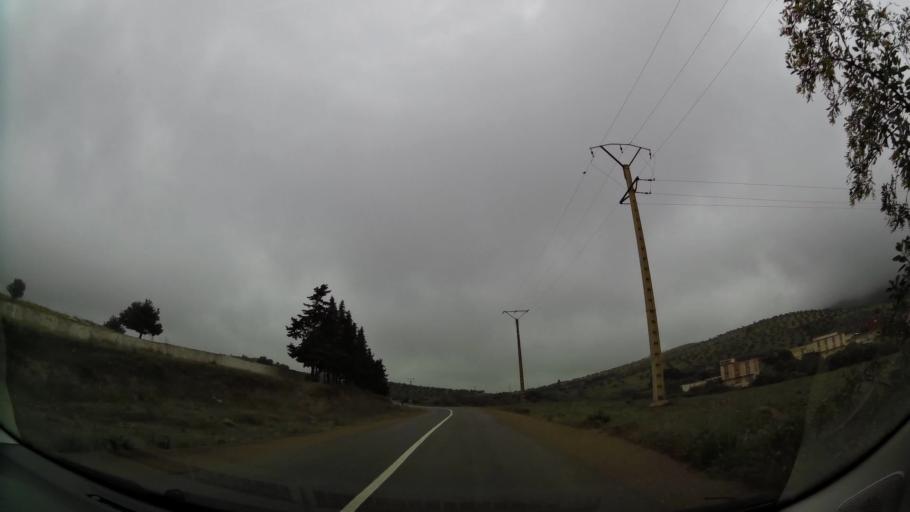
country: MA
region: Oriental
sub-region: Nador
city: Selouane
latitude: 35.1253
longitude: -3.0608
